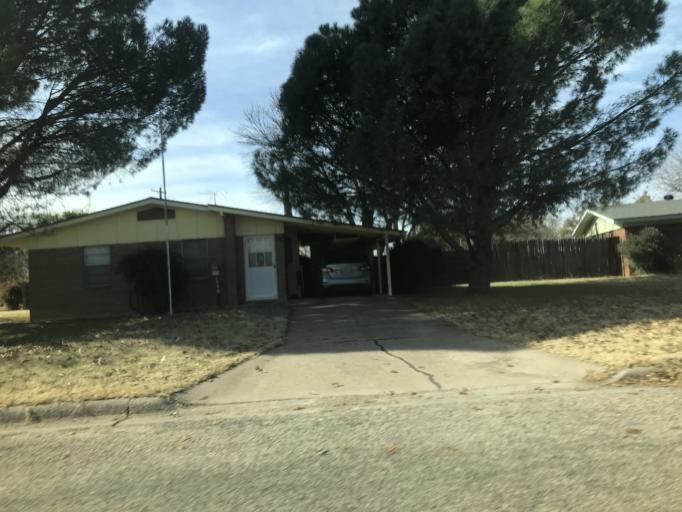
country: US
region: Texas
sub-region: Taylor County
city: Abilene
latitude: 32.4787
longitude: -99.7140
